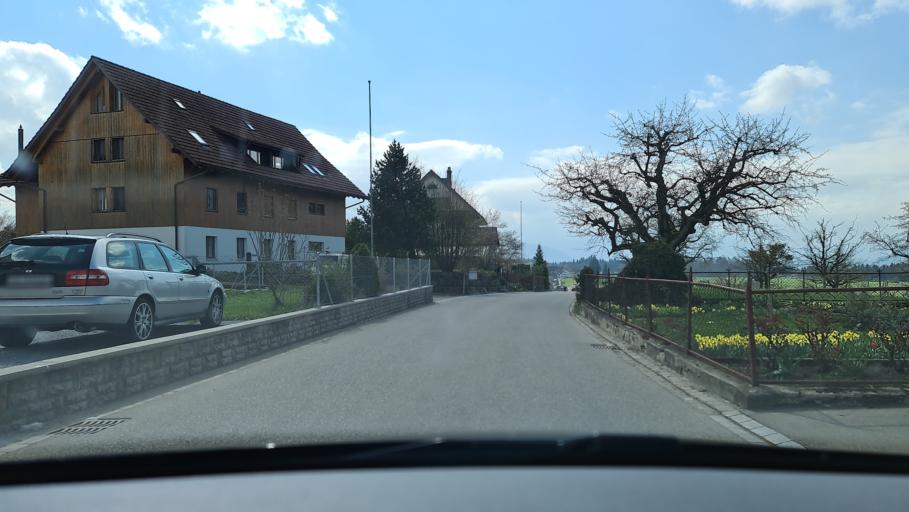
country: CH
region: Zurich
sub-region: Bezirk Affoltern
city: Knonau
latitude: 47.2298
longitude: 8.4957
